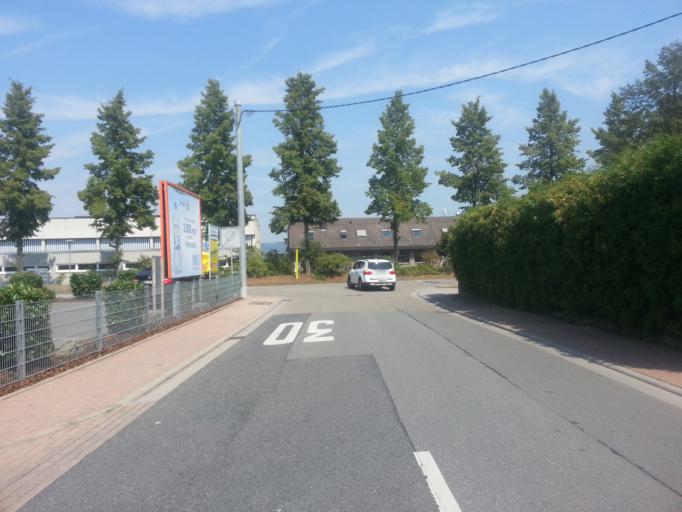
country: DE
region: Baden-Wuerttemberg
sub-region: Karlsruhe Region
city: Edingen-Neckarhausen
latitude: 49.4440
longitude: 8.6181
